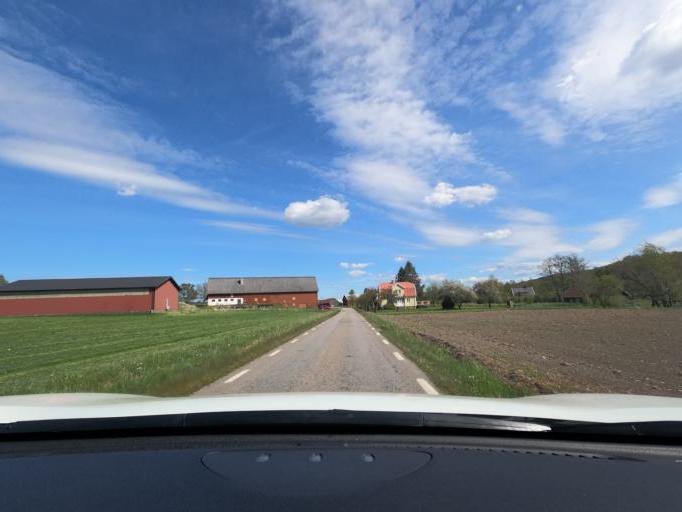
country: SE
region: Vaestra Goetaland
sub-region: Marks Kommun
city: Horred
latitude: 57.4499
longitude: 12.4732
